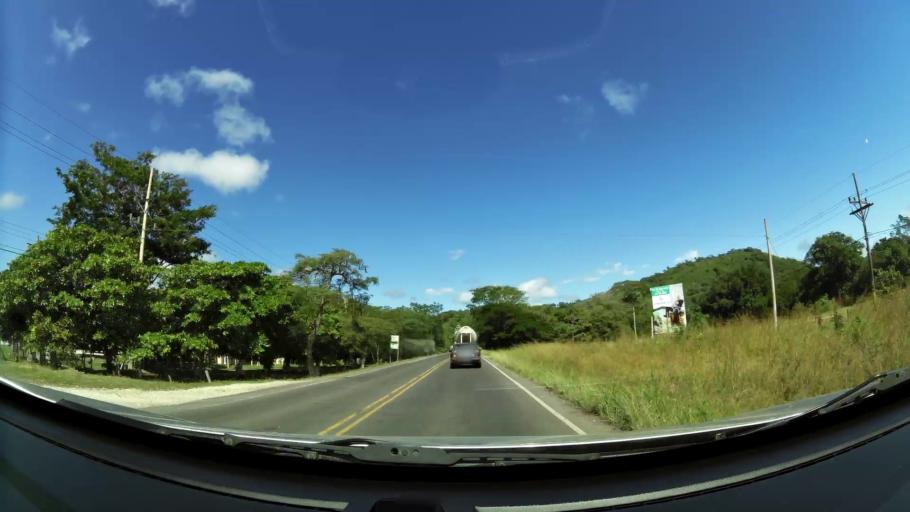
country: CR
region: Guanacaste
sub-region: Canton de Canas
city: Canas
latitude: 10.3983
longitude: -85.0808
